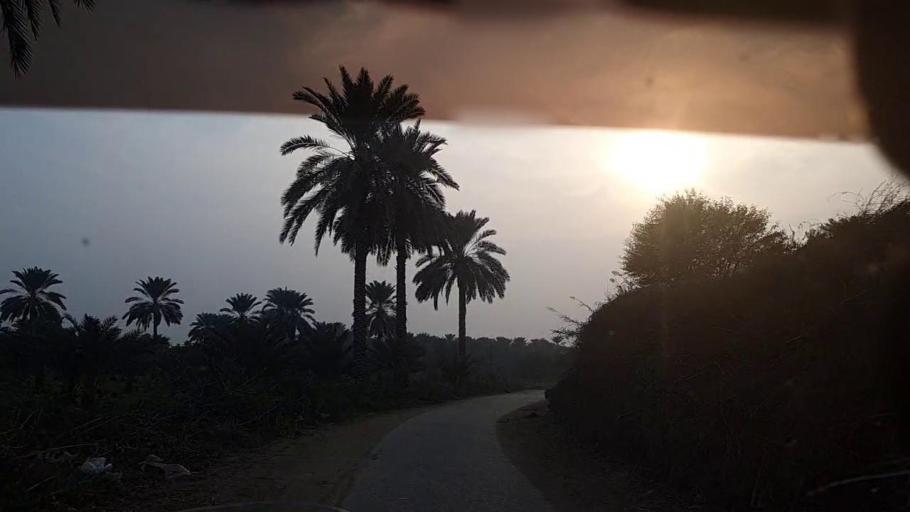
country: PK
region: Sindh
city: Khairpur
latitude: 27.4994
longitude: 68.6797
